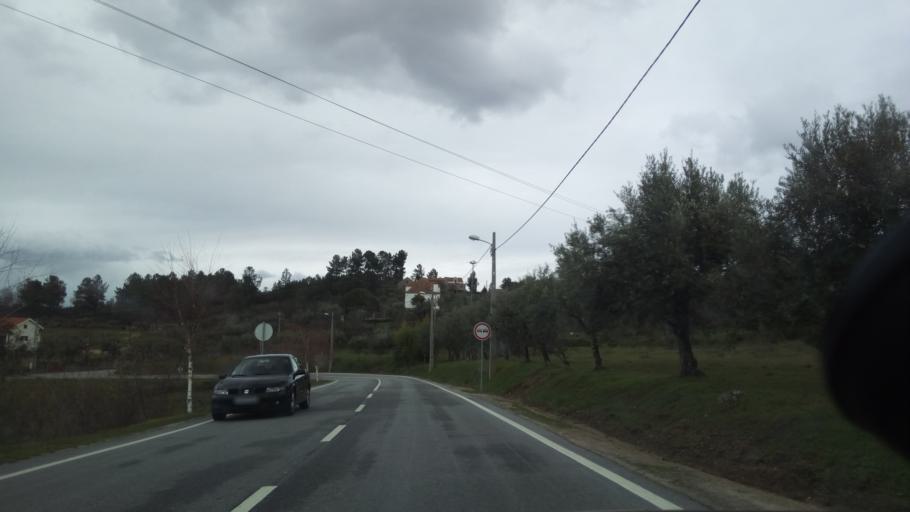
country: PT
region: Guarda
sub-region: Manteigas
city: Manteigas
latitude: 40.5028
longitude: -7.5843
